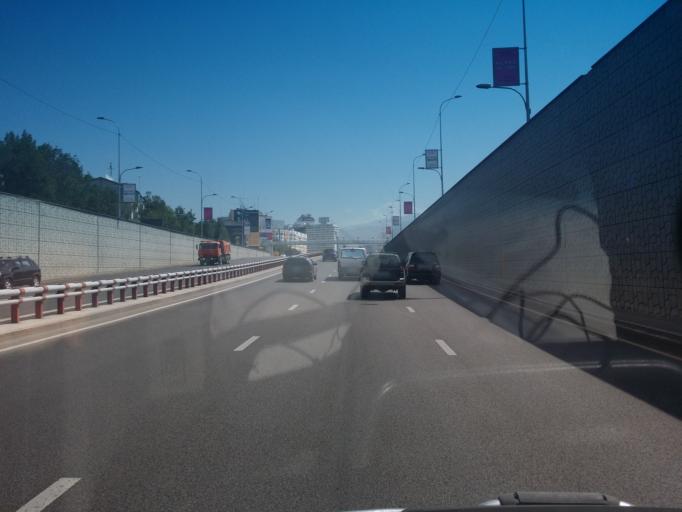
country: KZ
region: Almaty Qalasy
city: Almaty
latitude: 43.1947
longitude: 76.8830
